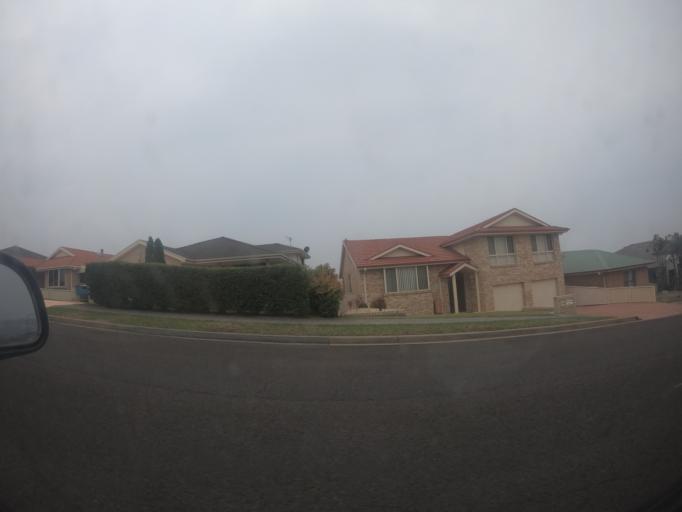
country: AU
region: New South Wales
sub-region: Shellharbour
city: Flinders
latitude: -34.5787
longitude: 150.8428
